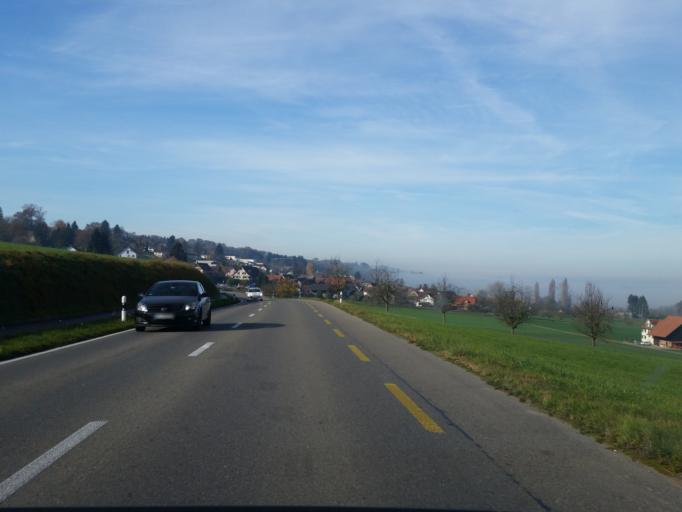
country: CH
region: Thurgau
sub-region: Kreuzlingen District
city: Tagerwilen
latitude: 47.6600
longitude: 9.1182
